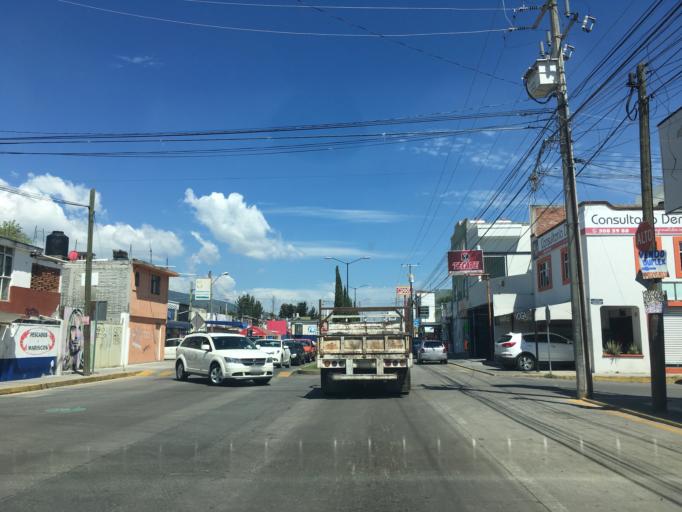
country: MX
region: Michoacan
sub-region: Morelia
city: Morelos
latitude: 19.6847
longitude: -101.2257
